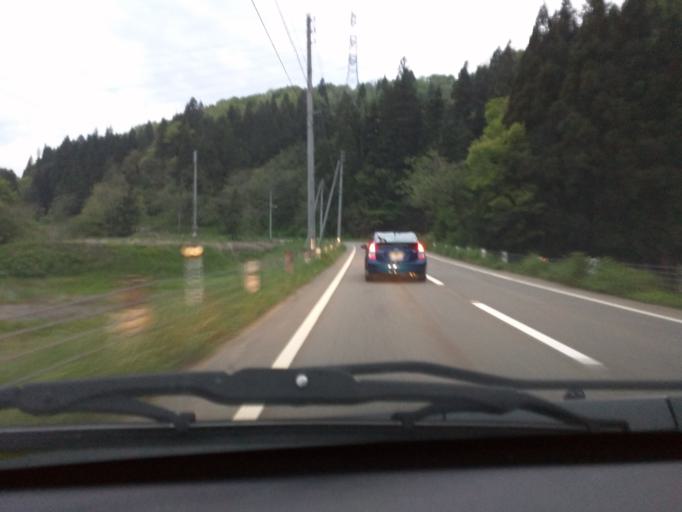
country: JP
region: Niigata
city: Ojiya
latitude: 37.3214
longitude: 138.6913
